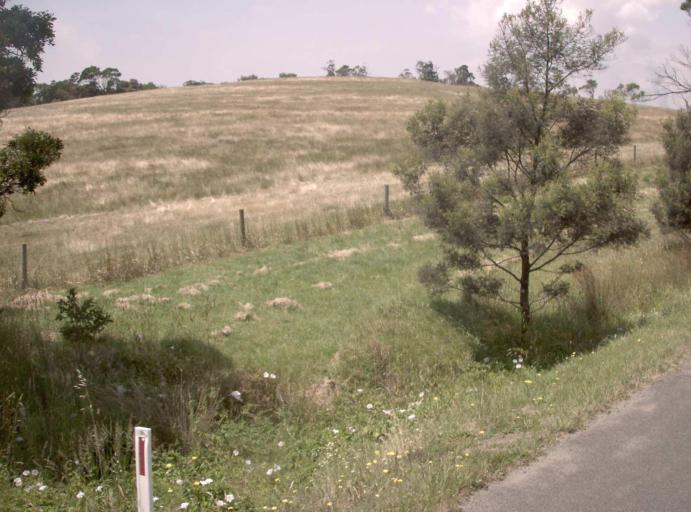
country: AU
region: Victoria
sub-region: Latrobe
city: Traralgon
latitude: -38.2150
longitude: 146.5465
